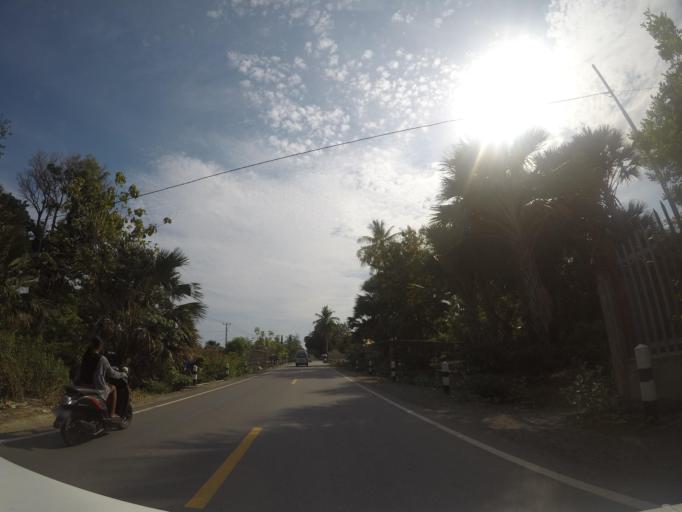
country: ID
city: Metinaro
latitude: -8.5402
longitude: 125.6806
